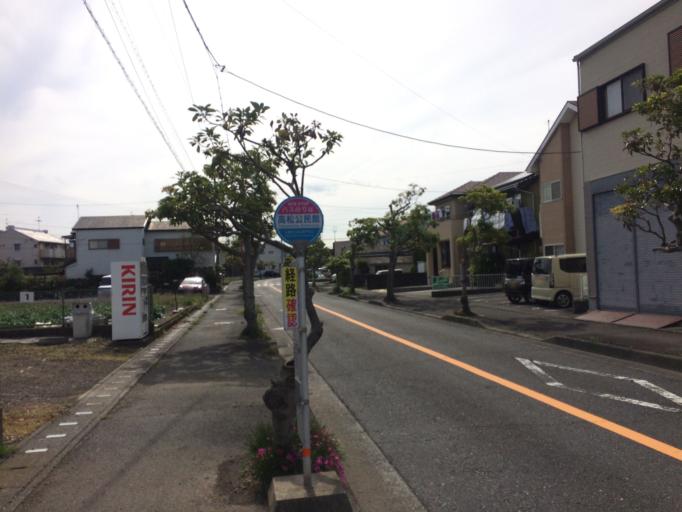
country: JP
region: Shizuoka
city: Shizuoka-shi
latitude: 34.9488
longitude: 138.4244
